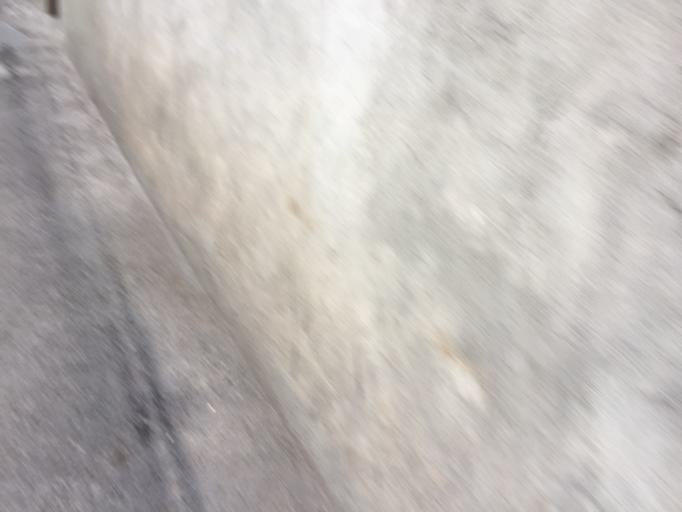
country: AM
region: Yerevan
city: Yerevan
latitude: 40.1895
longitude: 44.5148
